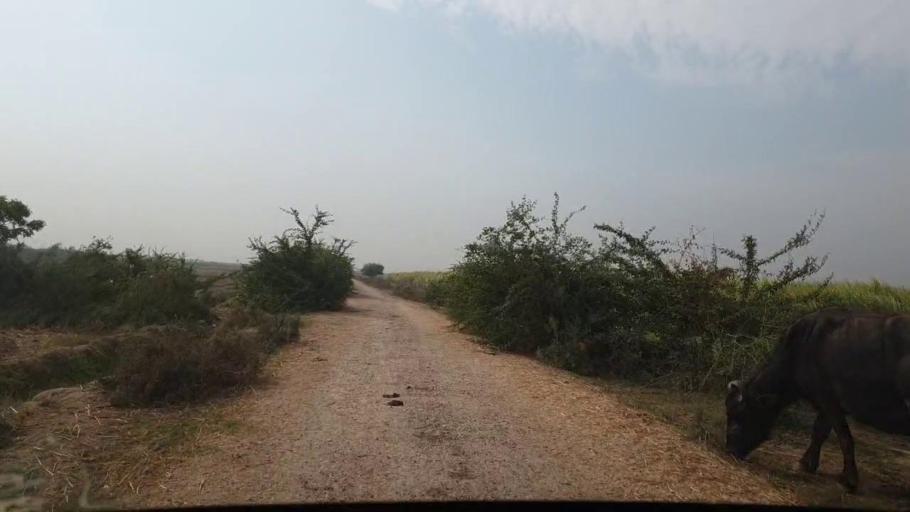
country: PK
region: Sindh
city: Chuhar Jamali
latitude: 24.4132
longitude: 67.9387
